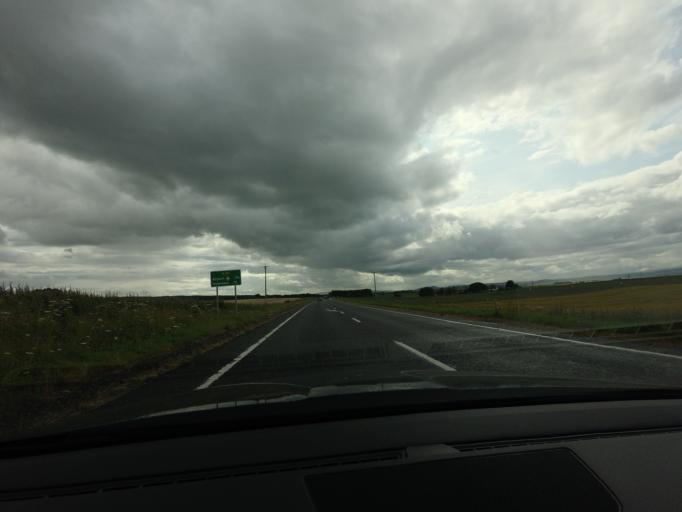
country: GB
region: Scotland
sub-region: Highland
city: Fortrose
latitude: 57.5434
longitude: -4.0072
